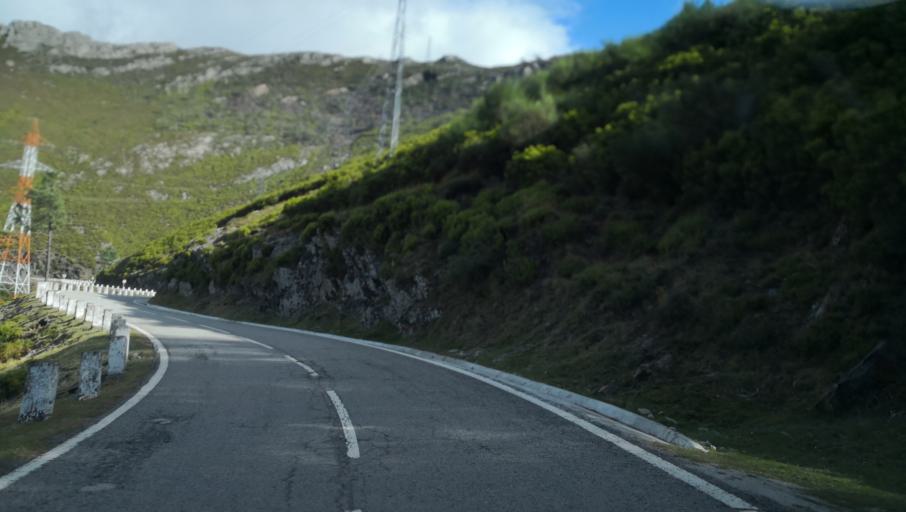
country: PT
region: Vila Real
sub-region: Mondim de Basto
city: Mondim de Basto
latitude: 41.3246
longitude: -7.8785
